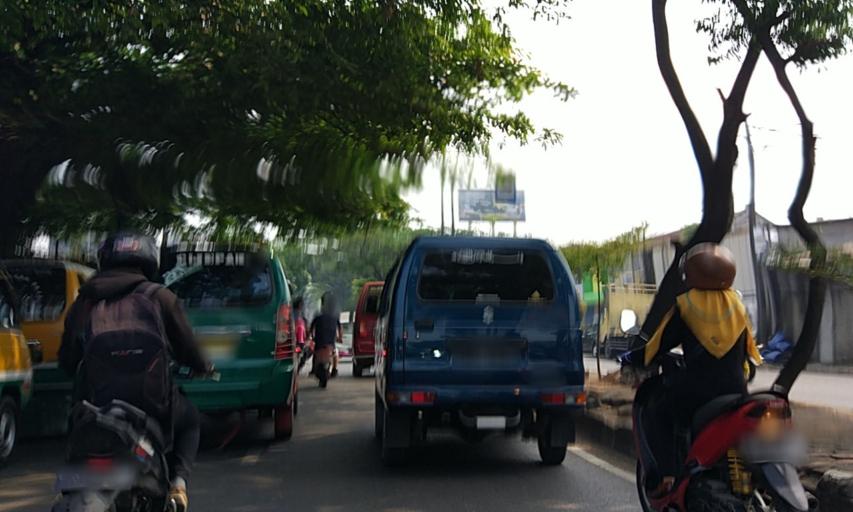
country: ID
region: West Java
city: Bandung
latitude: -6.9144
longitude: 107.5714
